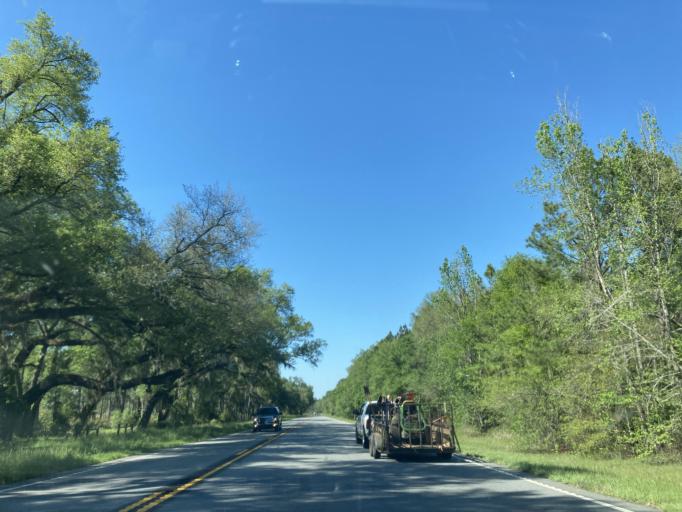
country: US
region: Georgia
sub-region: Baker County
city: Newton
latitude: 31.4199
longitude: -84.2771
